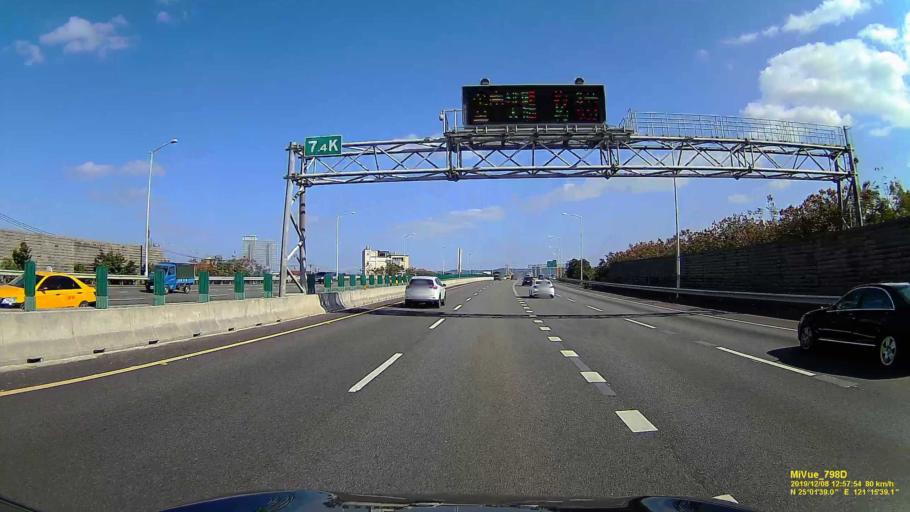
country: TW
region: Taiwan
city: Taoyuan City
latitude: 25.0272
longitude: 121.2614
